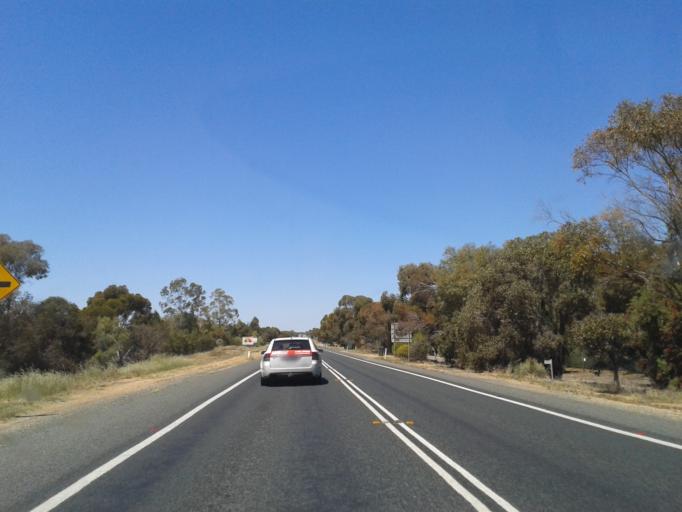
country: AU
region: New South Wales
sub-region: Wentworth
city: Gol Gol
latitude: -34.1868
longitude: 142.2322
